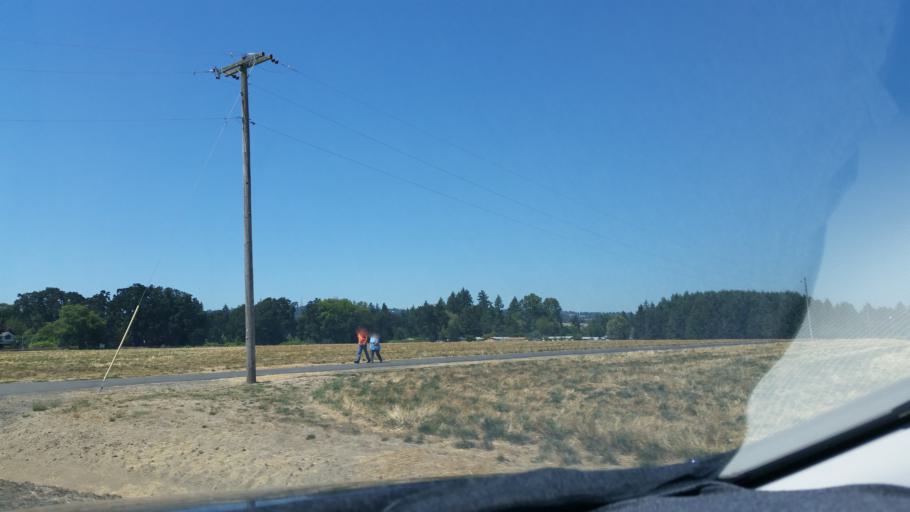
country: US
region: Oregon
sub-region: Clackamas County
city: Wilsonville
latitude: 45.2596
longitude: -122.8188
